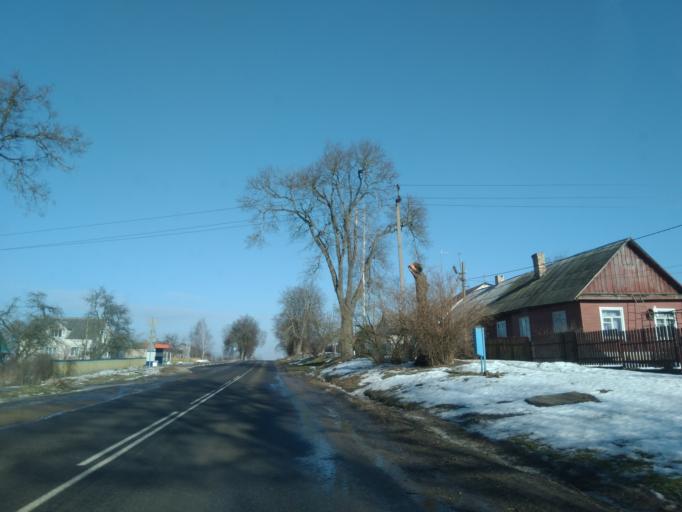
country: BY
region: Minsk
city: Nyasvizh
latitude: 53.2059
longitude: 26.6602
